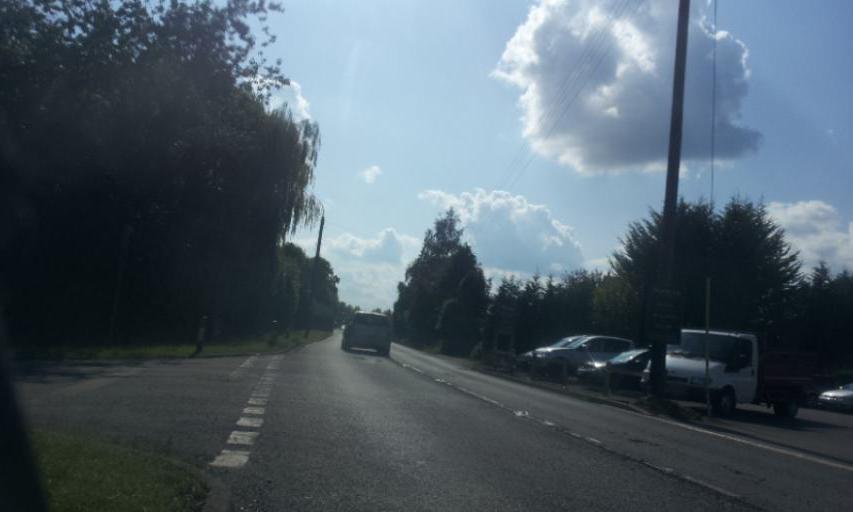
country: GB
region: England
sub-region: Kent
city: Yalding
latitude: 51.2308
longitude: 0.4059
